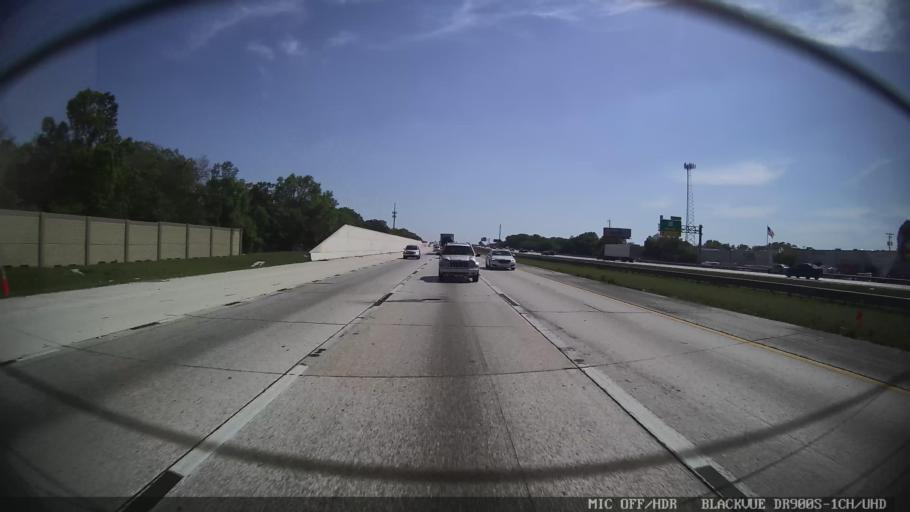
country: US
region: Florida
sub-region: Hillsborough County
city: Mango
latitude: 27.9571
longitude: -82.3261
